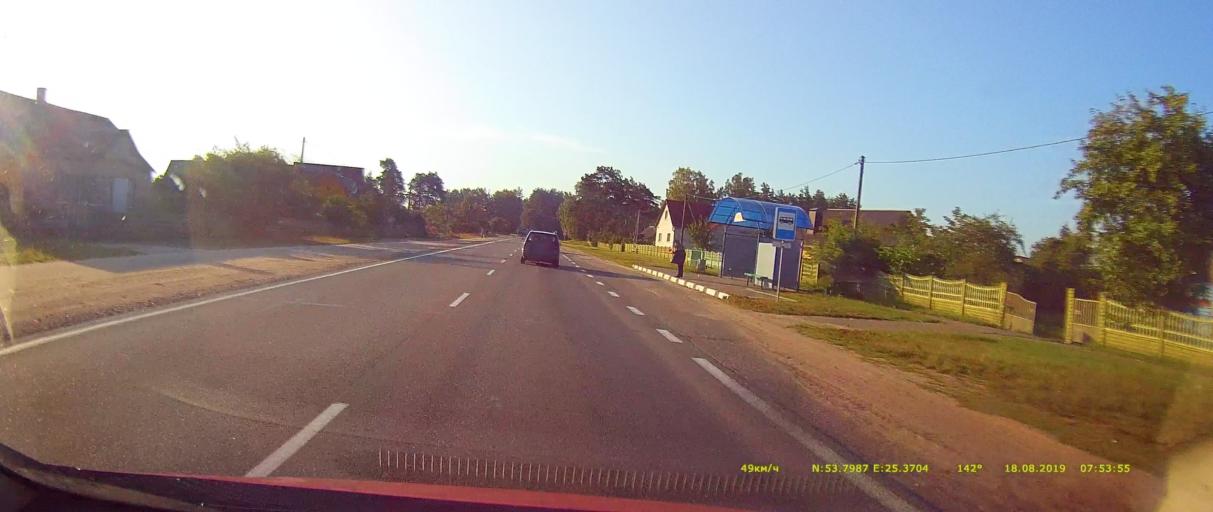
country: BY
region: Grodnenskaya
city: Dzyatlava
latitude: 53.4708
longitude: 25.4059
